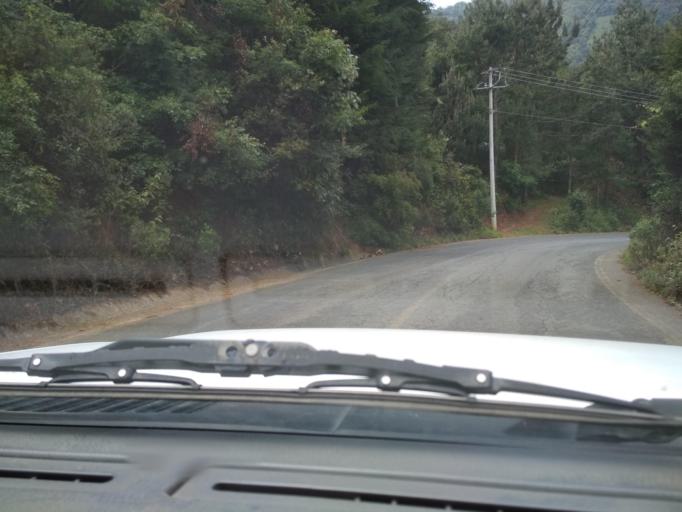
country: MX
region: Veracruz
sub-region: Camerino Z. Mendoza
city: La Cuesta
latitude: 18.7897
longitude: -97.1575
